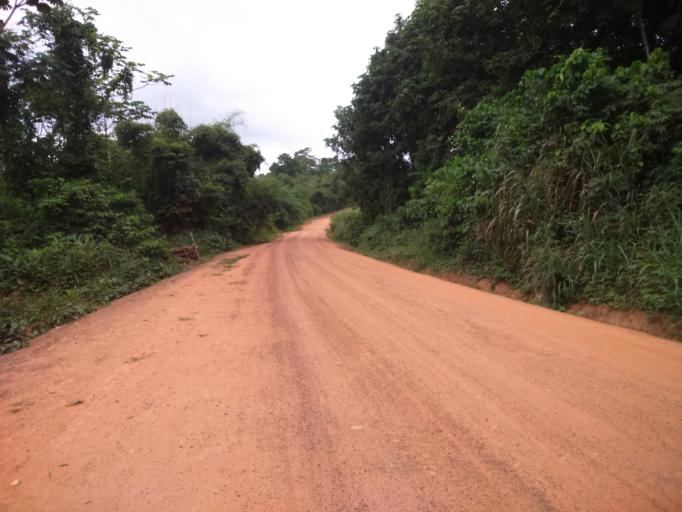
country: CI
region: Lagunes
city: Agou
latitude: 6.0852
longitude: -4.0668
